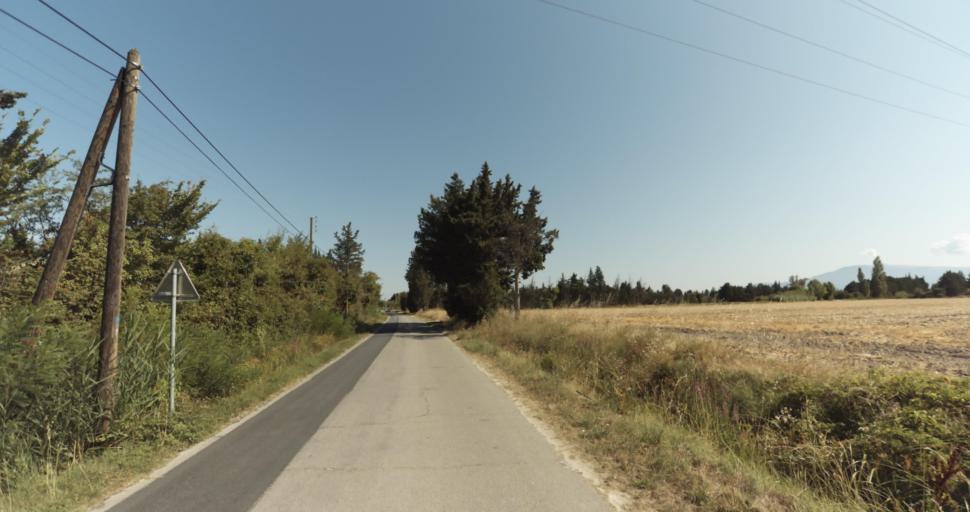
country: FR
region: Provence-Alpes-Cote d'Azur
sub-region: Departement du Vaucluse
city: Monteux
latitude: 44.0195
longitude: 4.9912
